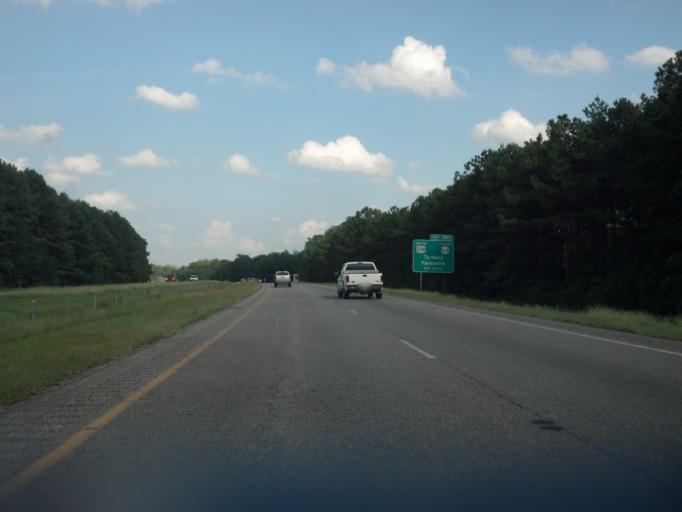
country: US
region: North Carolina
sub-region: Edgecombe County
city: Tarboro
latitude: 35.8829
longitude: -77.5693
